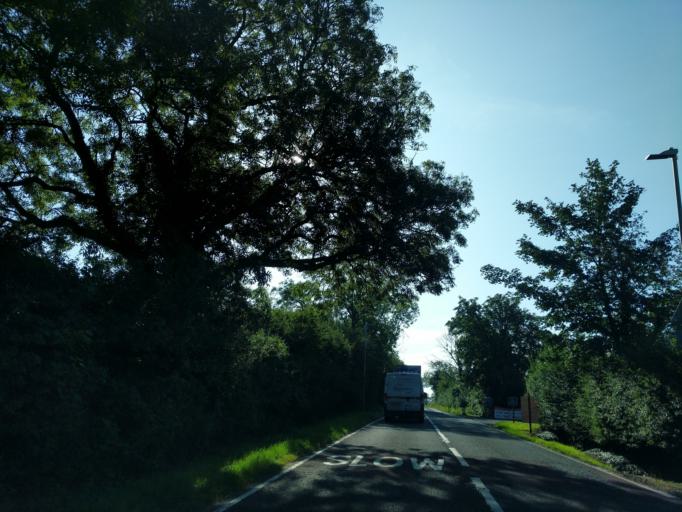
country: GB
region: England
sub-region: District of Rutland
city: Clipsham
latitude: 52.8099
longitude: -0.5132
